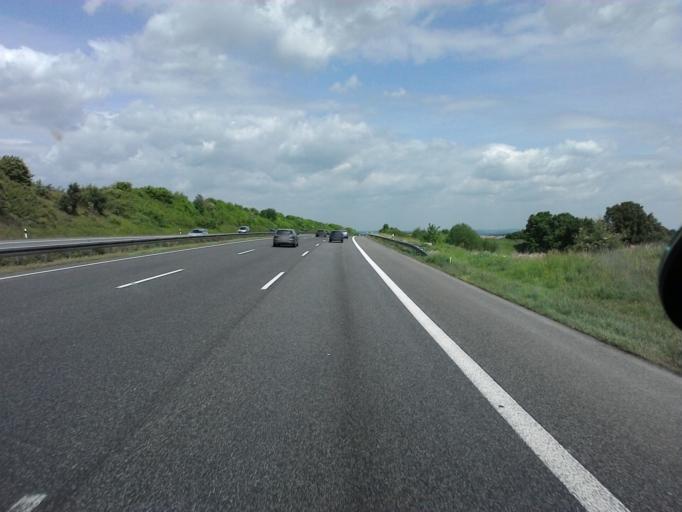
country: DE
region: North Rhine-Westphalia
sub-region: Regierungsbezirk Koln
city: Konigswinter
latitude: 50.7130
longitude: 7.2435
